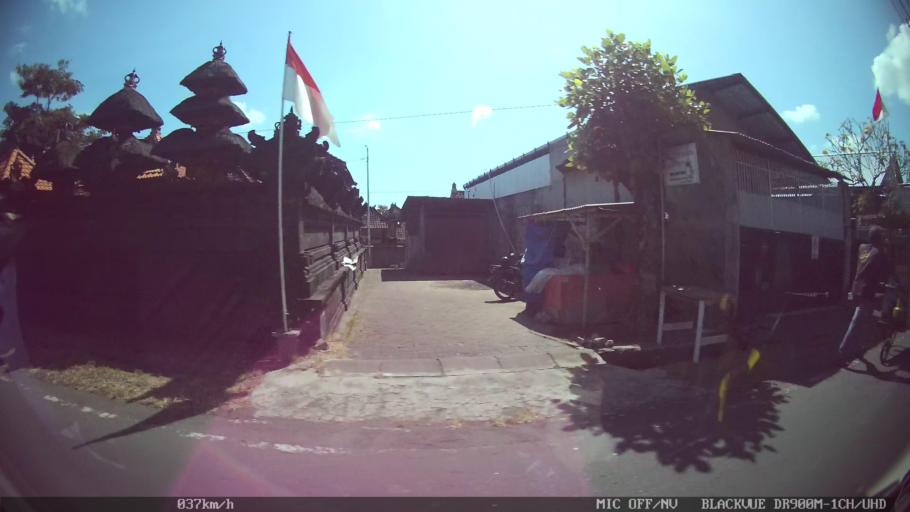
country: ID
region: Bali
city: Denpasar
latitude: -8.6509
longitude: 115.1781
